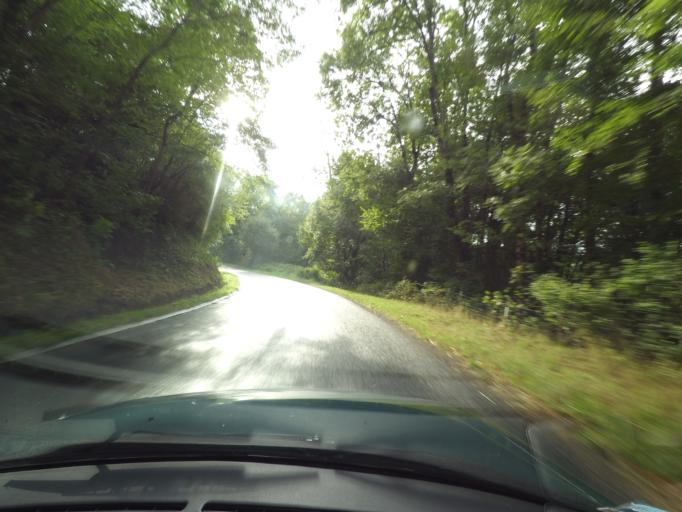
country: FR
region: Limousin
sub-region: Departement de la Haute-Vienne
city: Sereilhac
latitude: 45.7428
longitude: 1.1228
